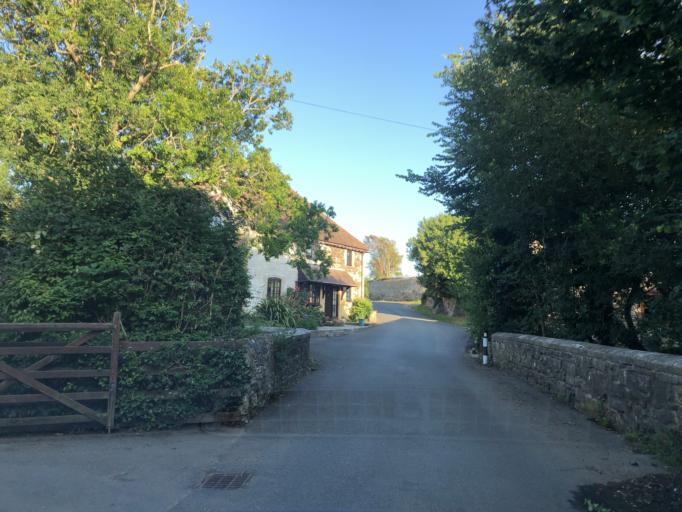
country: GB
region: England
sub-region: Isle of Wight
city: Shalfleet
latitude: 50.6391
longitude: -1.4004
